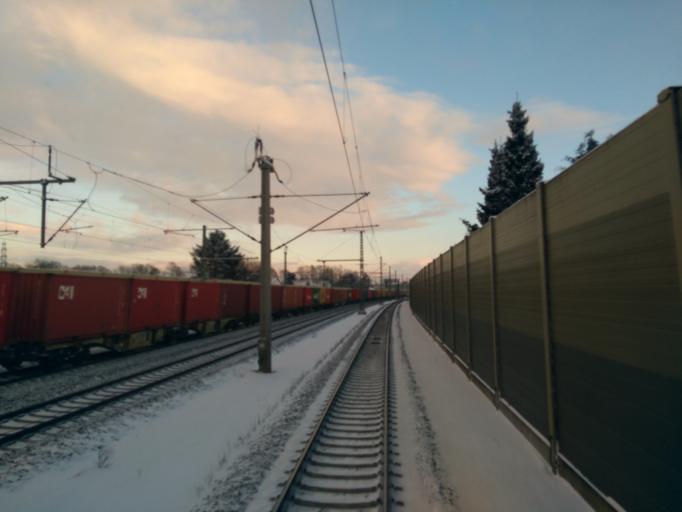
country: DE
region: Lower Saxony
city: Winsen
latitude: 53.3502
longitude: 10.2173
